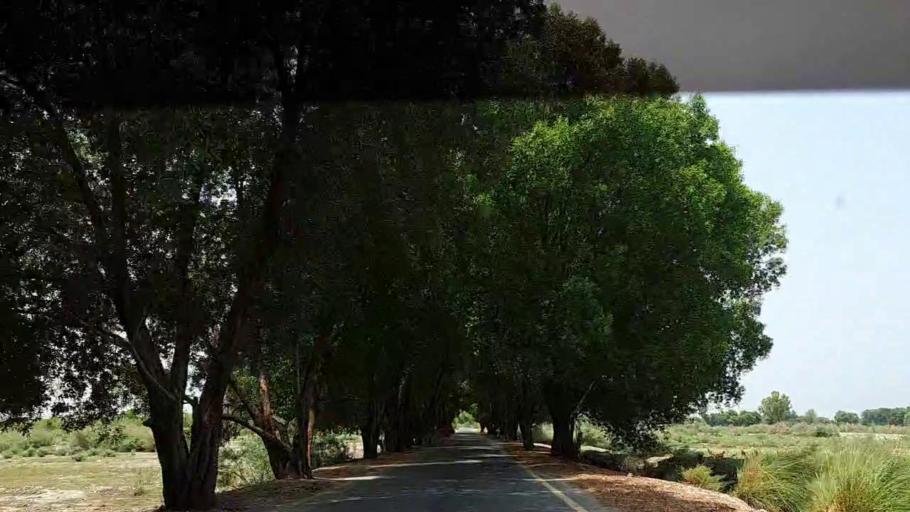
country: PK
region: Sindh
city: Adilpur
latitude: 27.8766
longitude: 69.2721
